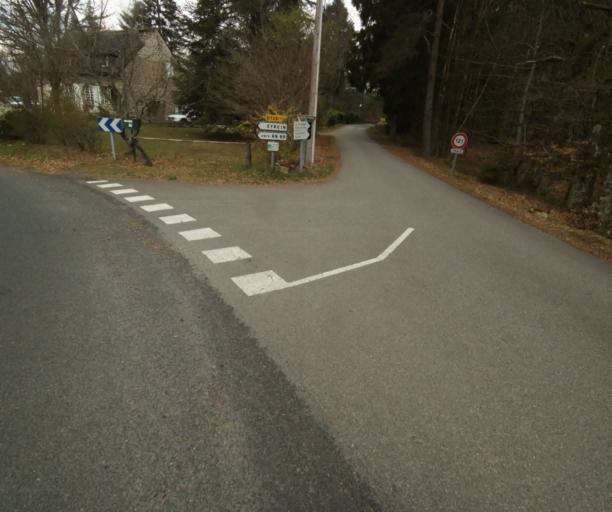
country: FR
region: Limousin
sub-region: Departement de la Correze
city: Correze
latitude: 45.3320
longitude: 1.9526
